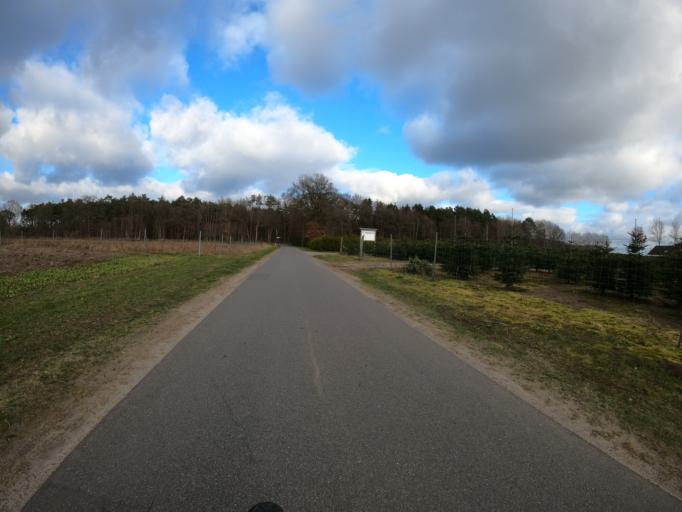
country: DE
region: Lower Saxony
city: Haselunne
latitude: 52.6634
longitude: 7.4419
